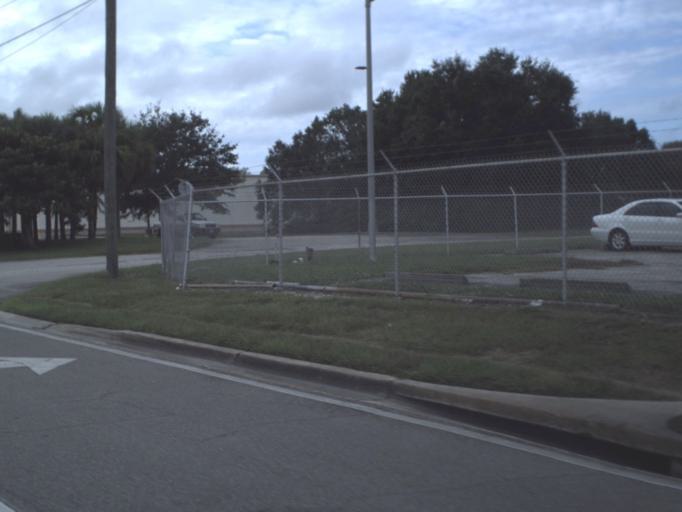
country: US
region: Florida
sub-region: Sarasota County
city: Venice Gardens
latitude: 27.0810
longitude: -82.4251
